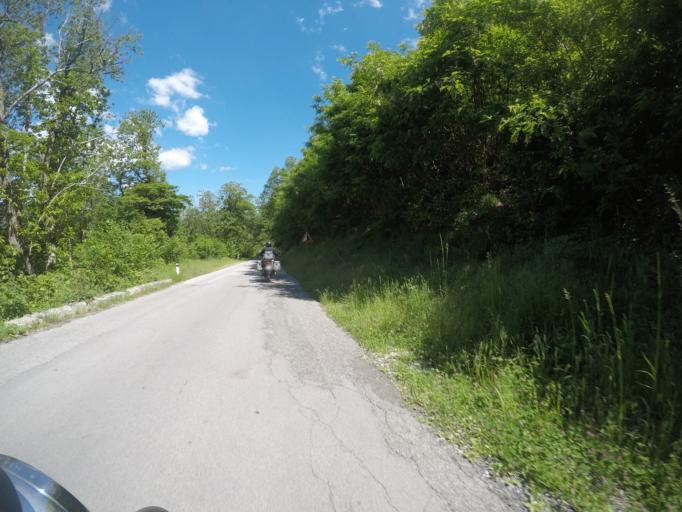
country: IT
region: Tuscany
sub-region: Provincia di Lucca
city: Careggine
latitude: 44.1278
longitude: 10.3361
